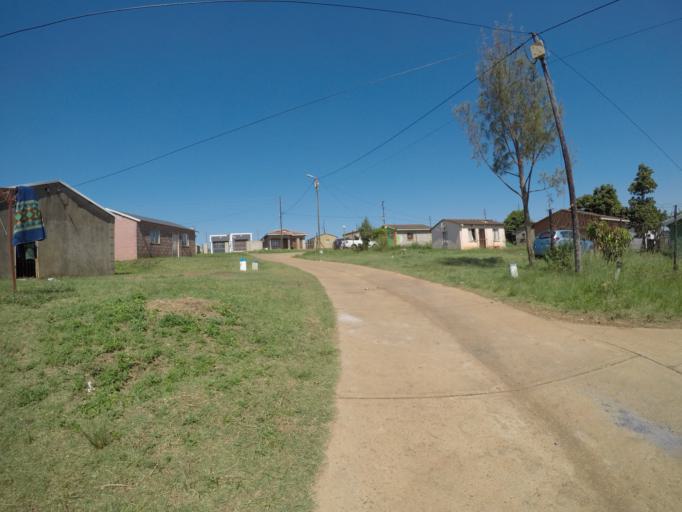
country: ZA
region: KwaZulu-Natal
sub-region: uThungulu District Municipality
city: Empangeni
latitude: -28.7684
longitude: 31.8763
